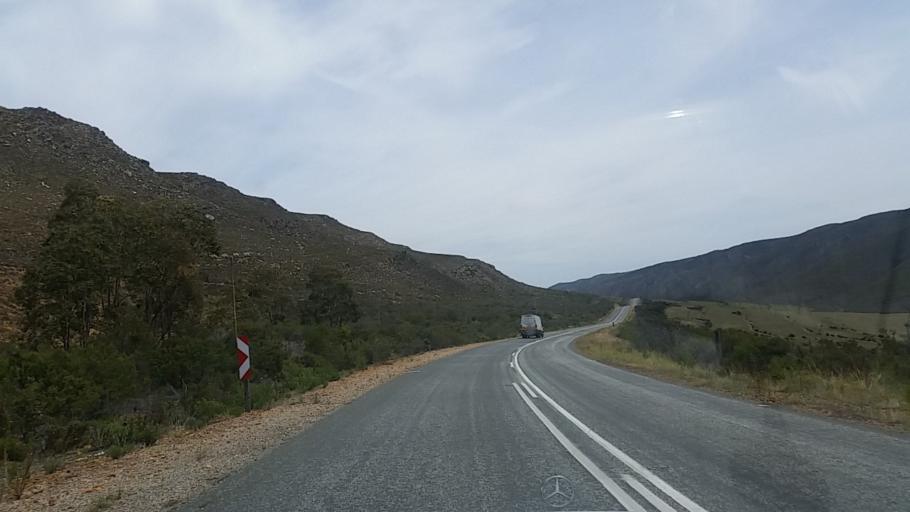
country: ZA
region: Western Cape
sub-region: Eden District Municipality
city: Knysna
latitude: -33.7428
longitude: 23.0220
